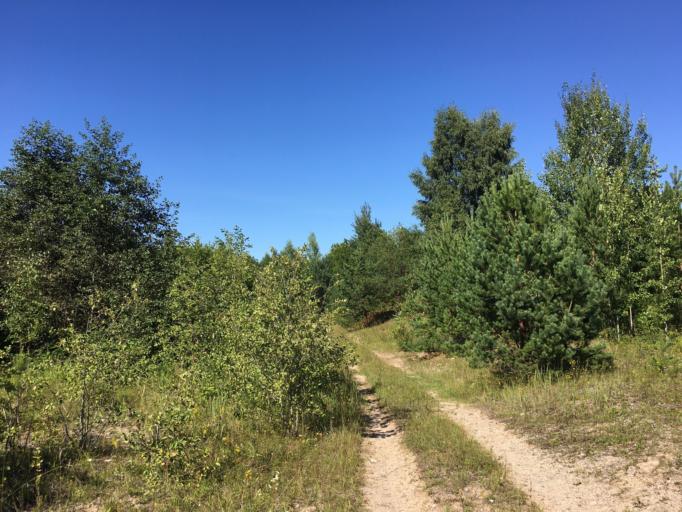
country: RU
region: Pskov
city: Izborsk
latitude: 57.8152
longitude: 27.9719
